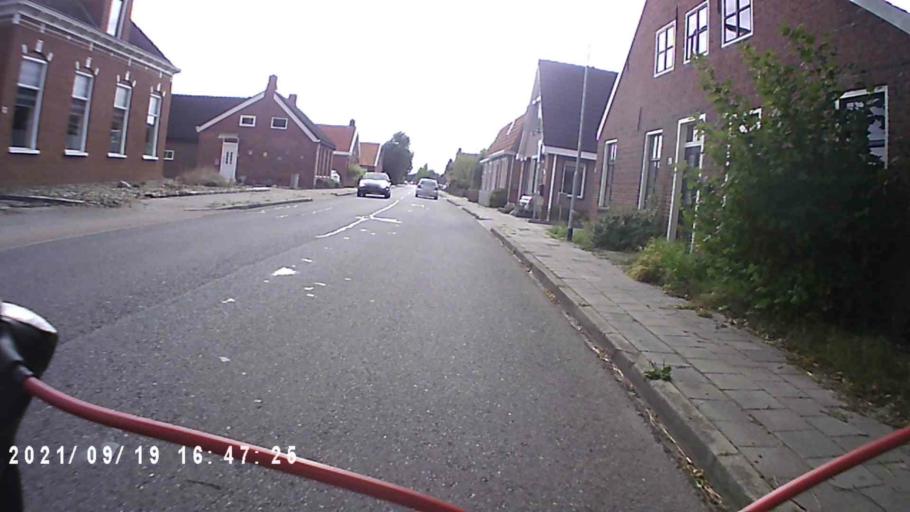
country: NL
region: Groningen
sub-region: Gemeente  Oldambt
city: Winschoten
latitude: 53.1773
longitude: 7.1006
